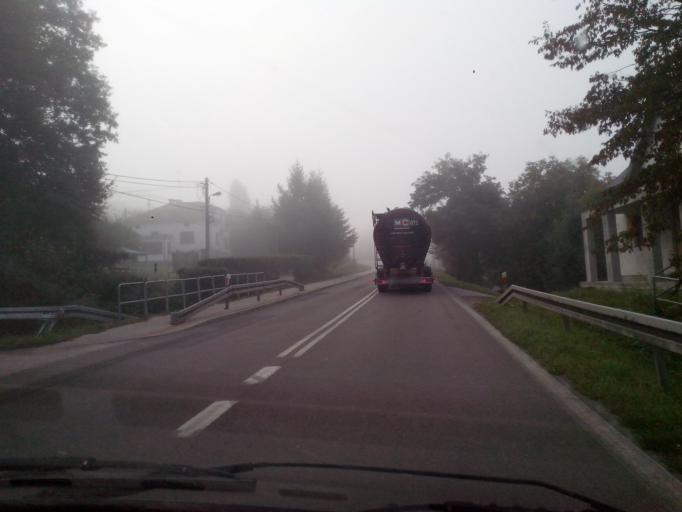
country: PL
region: Subcarpathian Voivodeship
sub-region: Przemysl
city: Przemysl
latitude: 49.8023
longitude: 22.7110
